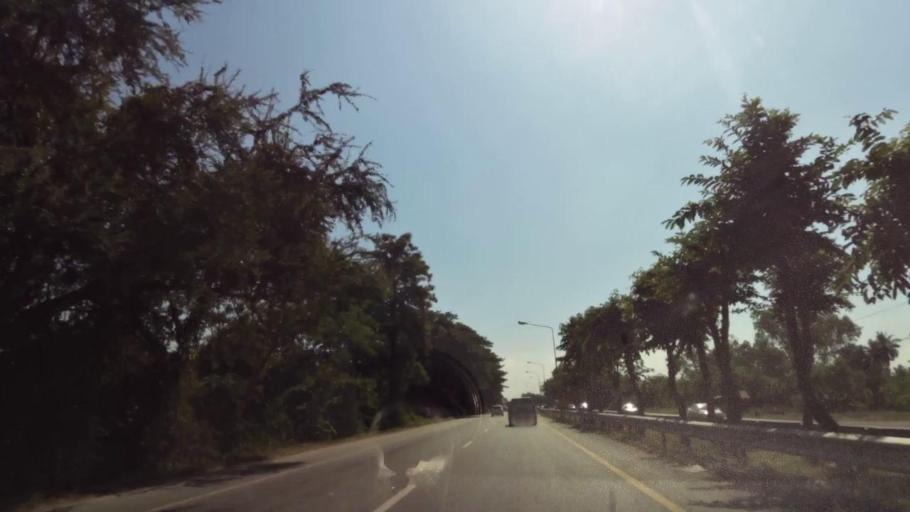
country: TH
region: Nakhon Sawan
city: Kao Liao
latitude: 15.7841
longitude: 100.1211
